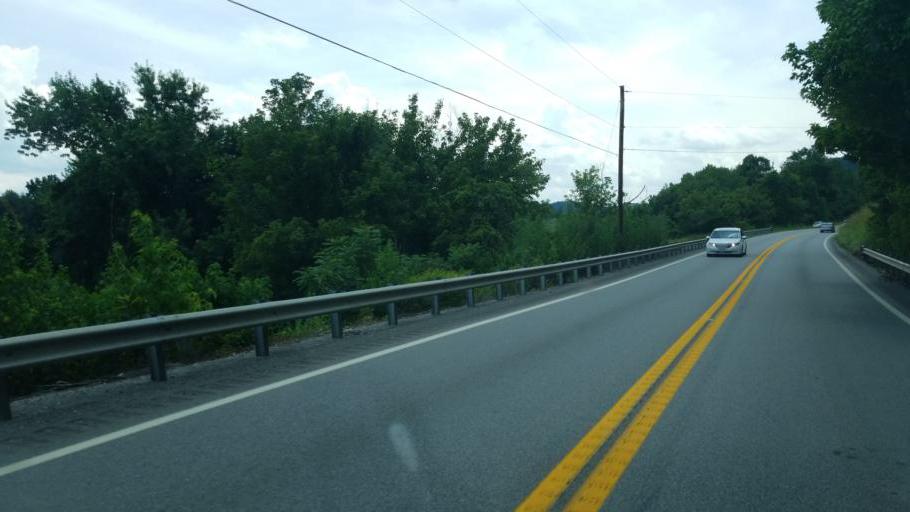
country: US
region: West Virginia
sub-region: Putnam County
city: Buffalo
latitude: 38.6101
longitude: -81.9960
